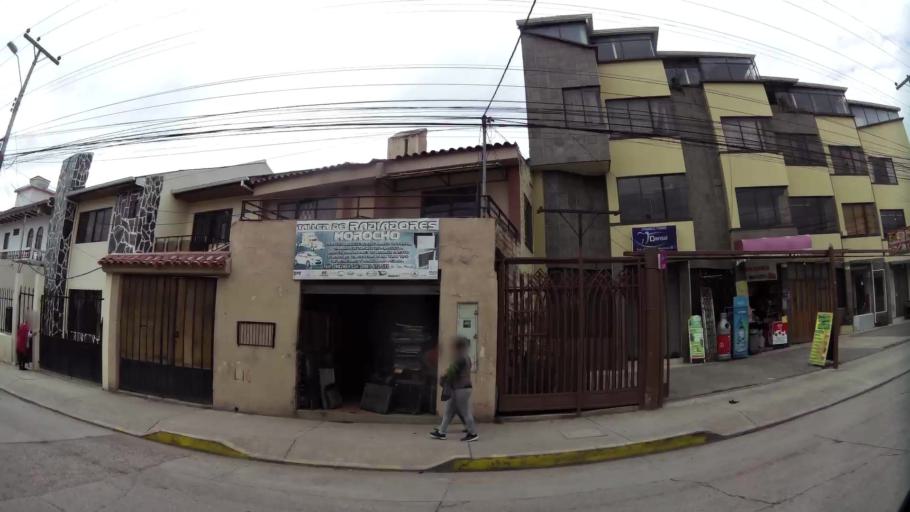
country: EC
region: Azuay
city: Cuenca
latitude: -2.9131
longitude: -79.0320
